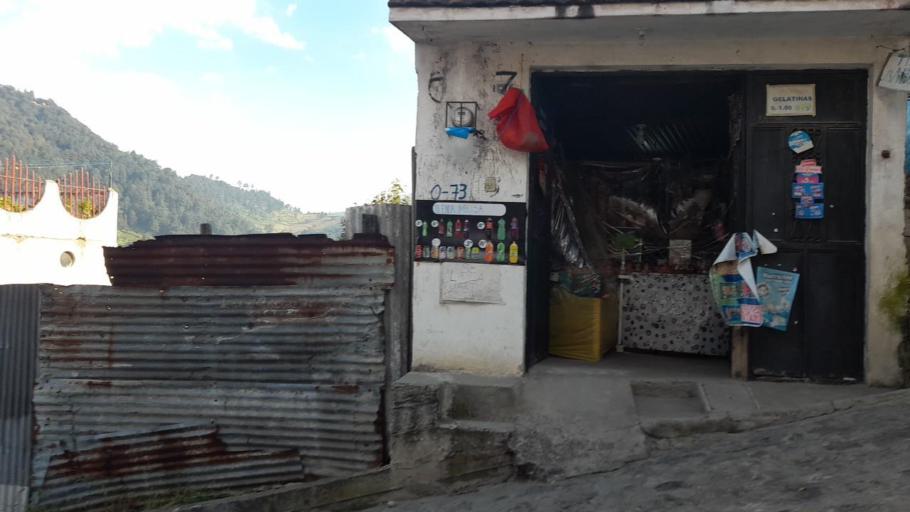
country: GT
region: Quetzaltenango
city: Quetzaltenango
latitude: 14.8387
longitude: -91.5121
